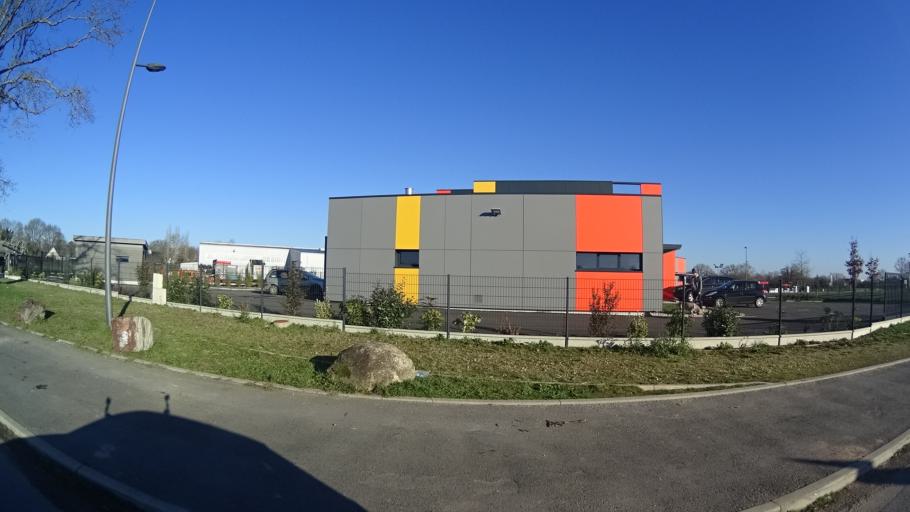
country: FR
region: Brittany
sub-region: Departement du Morbihan
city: Allaire
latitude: 47.6327
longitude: -2.1758
